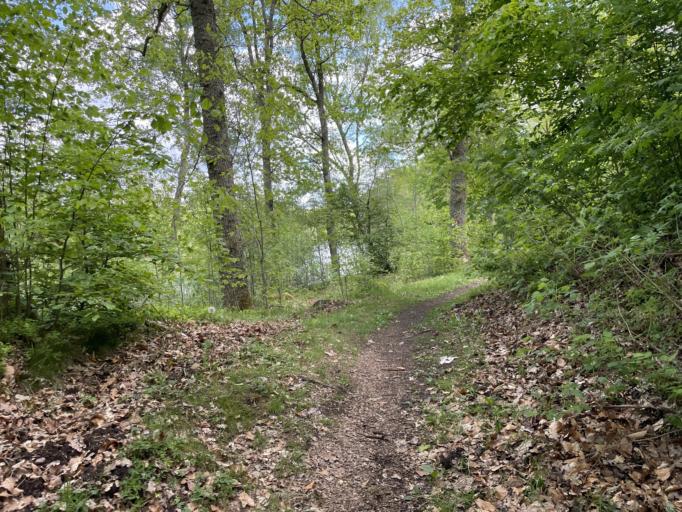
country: SE
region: Skane
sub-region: Klippans Kommun
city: Klippan
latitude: 56.1600
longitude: 13.1536
